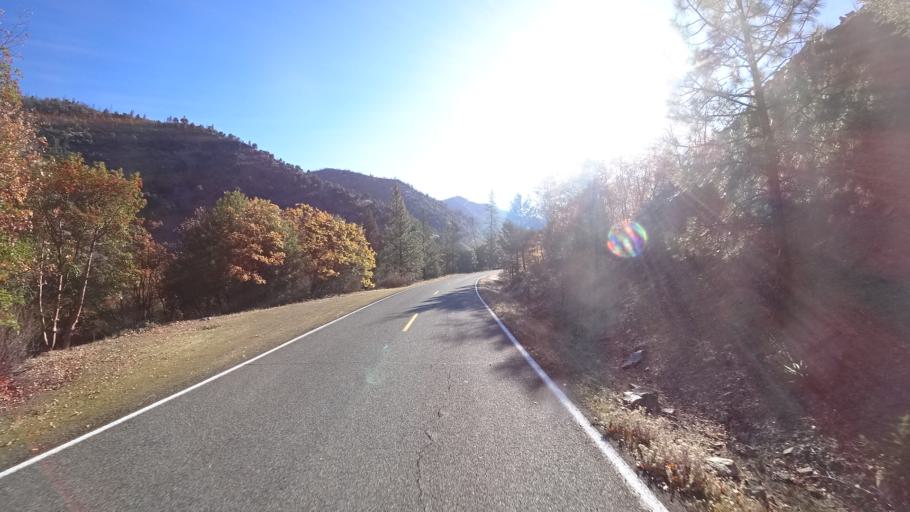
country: US
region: California
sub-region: Siskiyou County
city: Yreka
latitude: 41.9058
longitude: -122.8312
